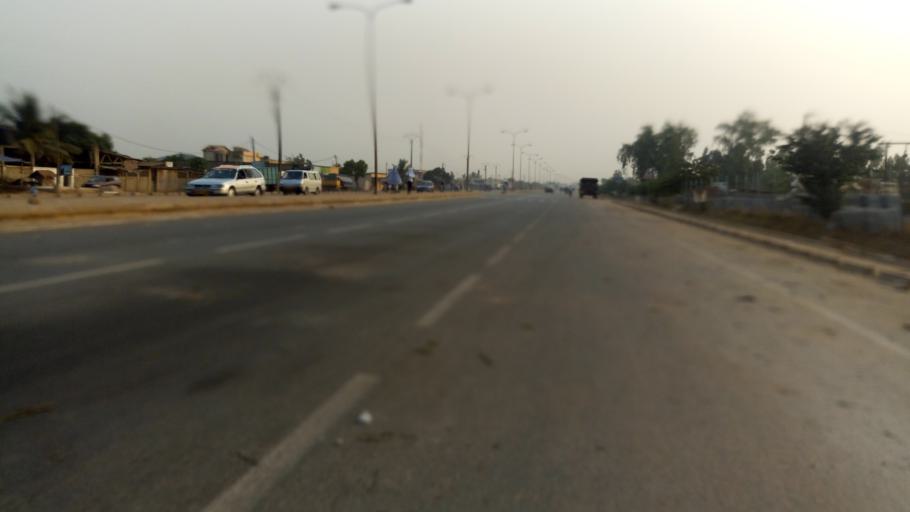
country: TG
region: Maritime
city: Lome
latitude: 6.2717
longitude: 1.2101
